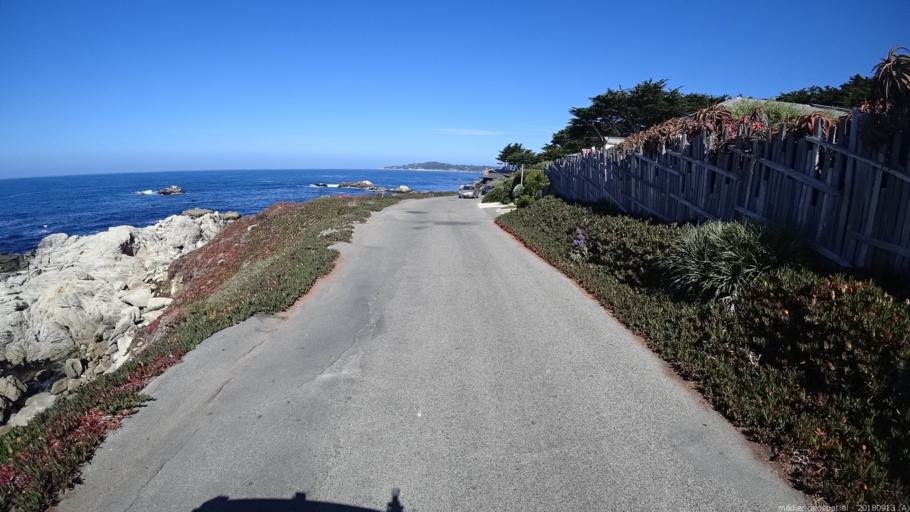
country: US
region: California
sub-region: Monterey County
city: Carmel-by-the-Sea
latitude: 36.5399
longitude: -121.9322
